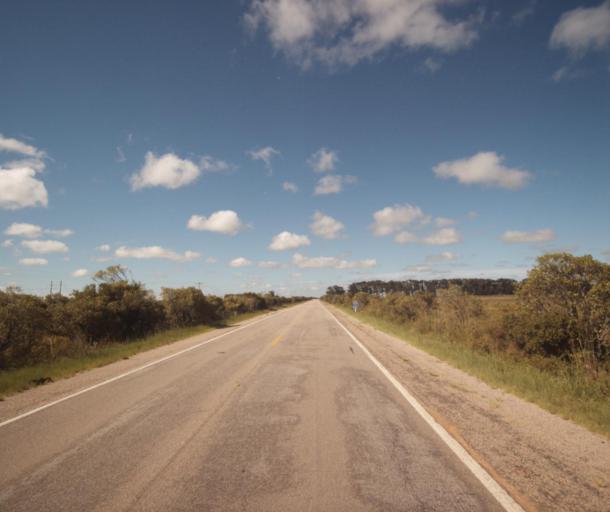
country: BR
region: Rio Grande do Sul
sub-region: Santa Vitoria Do Palmar
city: Santa Vitoria do Palmar
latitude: -33.4108
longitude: -53.2291
